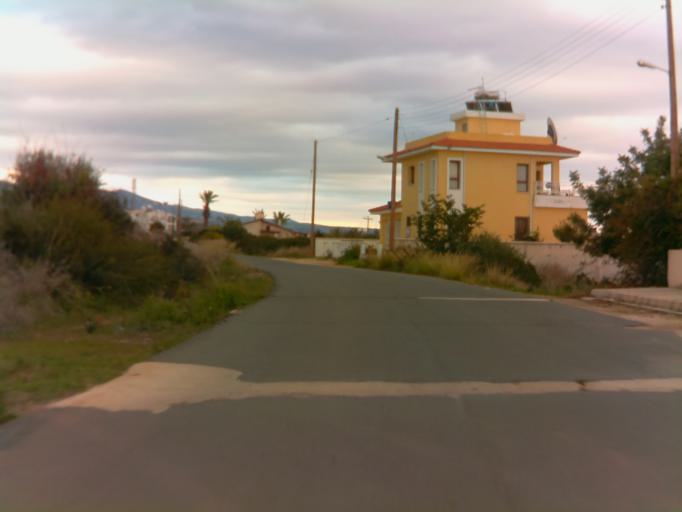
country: CY
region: Pafos
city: Pegeia
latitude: 34.8857
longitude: 32.3382
